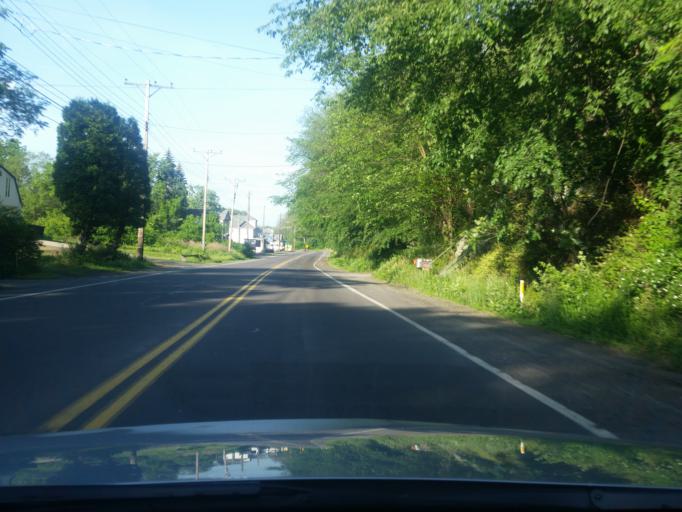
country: US
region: Pennsylvania
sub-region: Luzerne County
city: Plymouth
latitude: 41.2300
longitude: -75.9704
